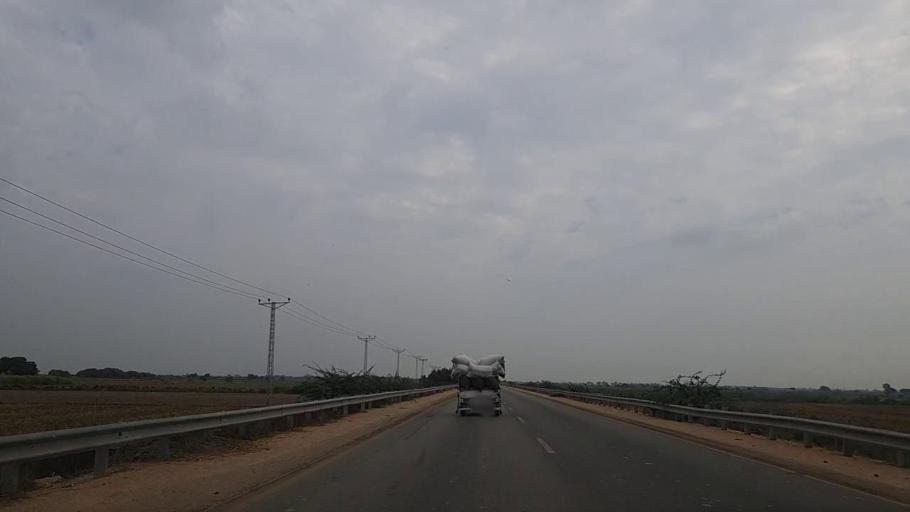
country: PK
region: Sindh
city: Thatta
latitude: 24.6165
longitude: 68.0650
